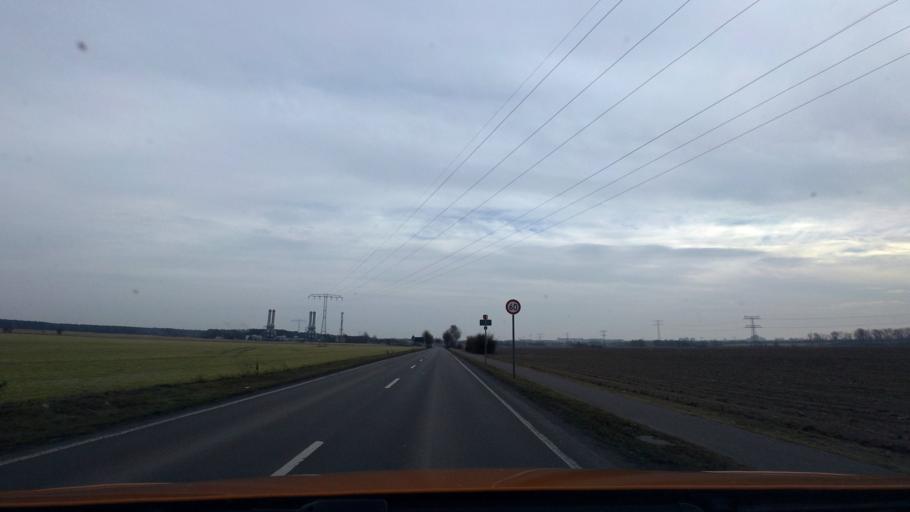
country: DE
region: Berlin
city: Falkenberg
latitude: 52.5927
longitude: 13.5473
